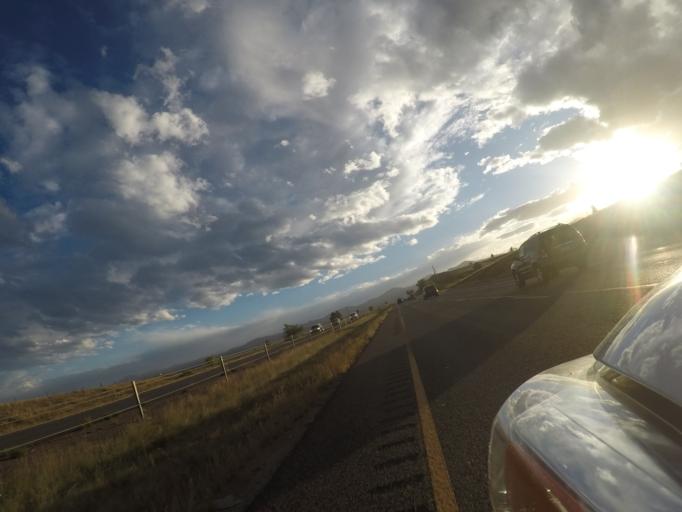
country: US
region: Colorado
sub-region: Jefferson County
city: Lakewood
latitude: 39.6509
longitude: -105.1214
